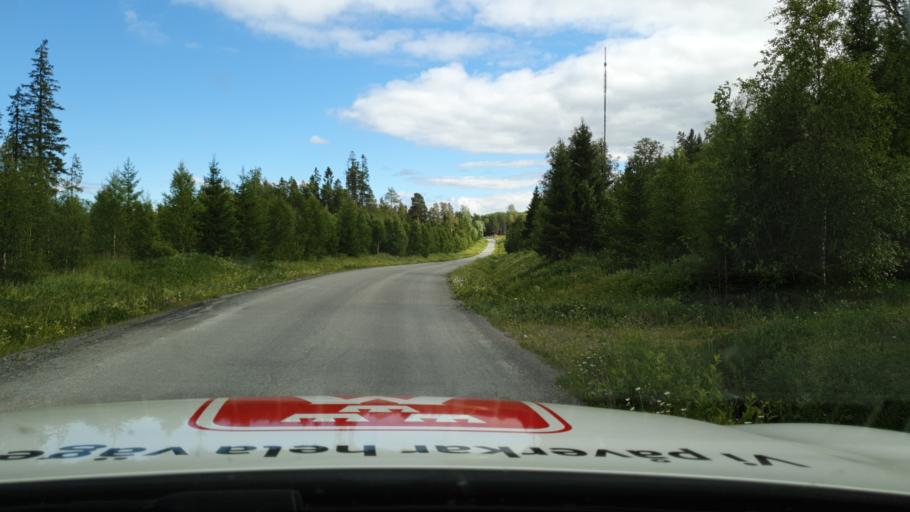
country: SE
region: Jaemtland
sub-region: OEstersunds Kommun
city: Ostersund
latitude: 63.1223
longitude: 14.5919
